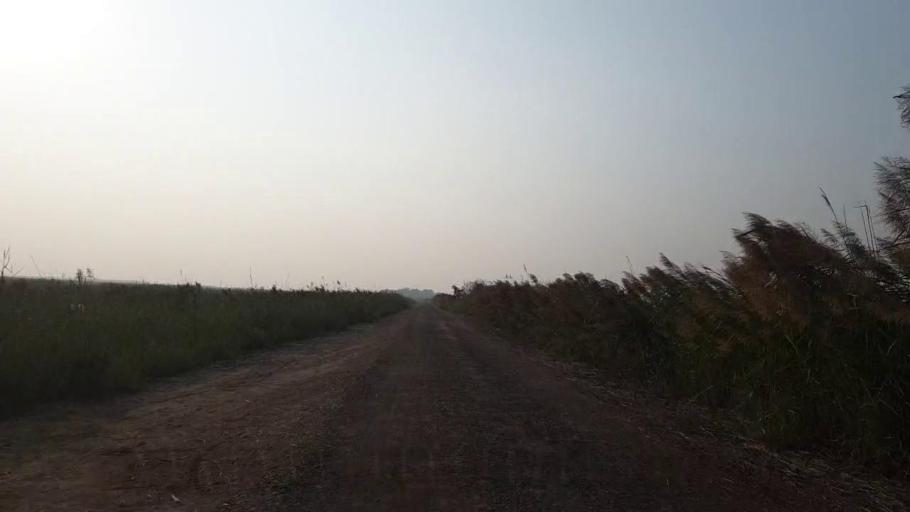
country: PK
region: Sindh
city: Bulri
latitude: 25.0852
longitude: 68.3170
